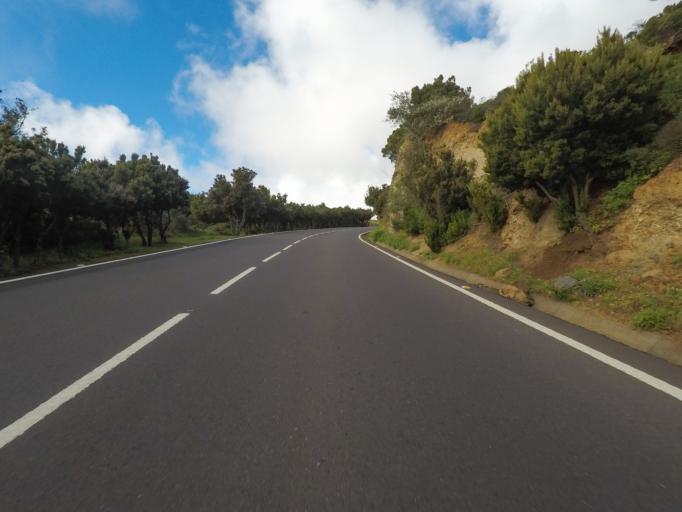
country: ES
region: Canary Islands
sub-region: Provincia de Santa Cruz de Tenerife
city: Alajero
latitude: 28.0999
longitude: -17.2002
